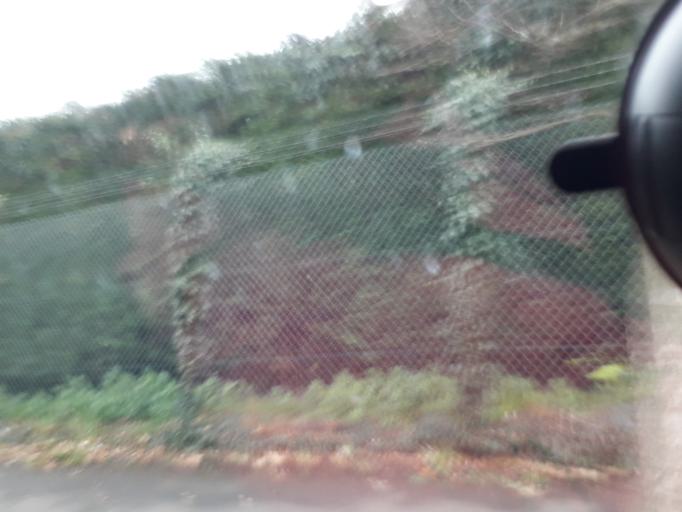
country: IE
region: Leinster
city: Donnybrook
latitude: 53.3160
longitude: -6.2184
